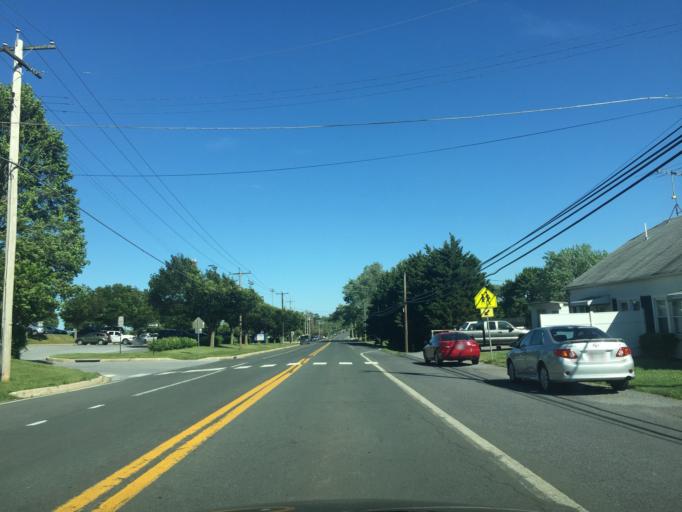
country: US
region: Maryland
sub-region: Carroll County
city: Westminster
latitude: 39.5215
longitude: -76.9206
